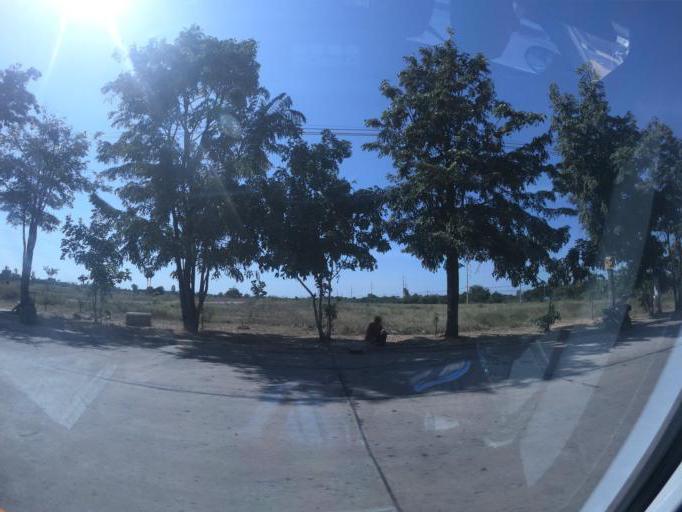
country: TH
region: Khon Kaen
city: Khon Kaen
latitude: 16.3906
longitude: 102.8034
